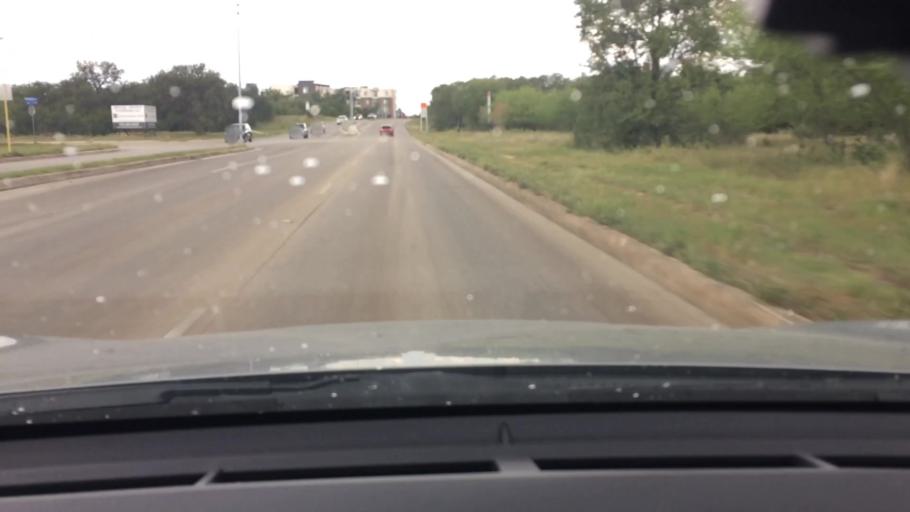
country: US
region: Texas
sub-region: Bexar County
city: Shavano Park
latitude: 29.5859
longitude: -98.5884
